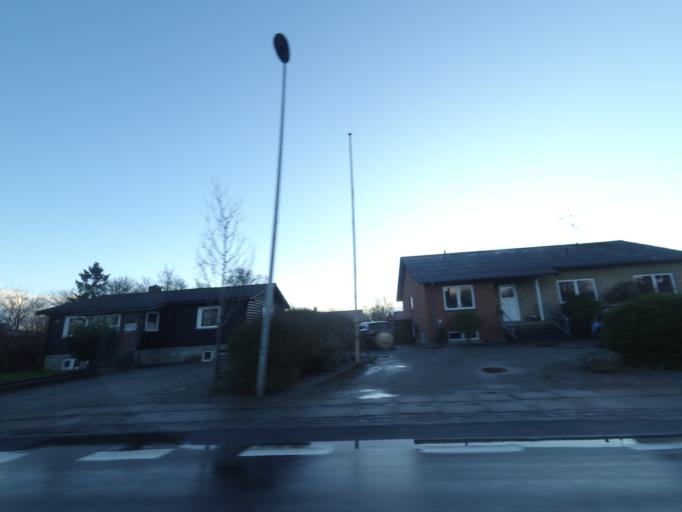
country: DK
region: Central Jutland
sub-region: Ikast-Brande Kommune
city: Brande
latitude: 56.0079
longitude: 9.1147
